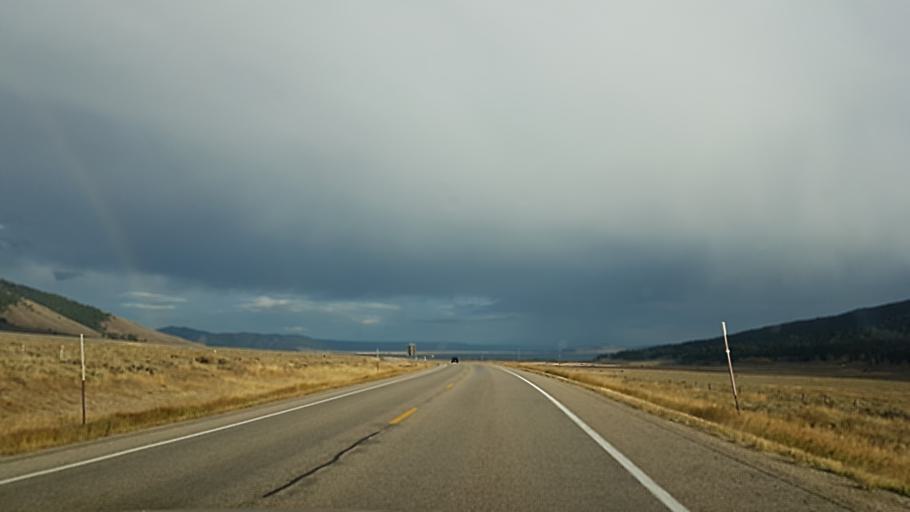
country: US
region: Montana
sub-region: Gallatin County
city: West Yellowstone
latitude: 44.6987
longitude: -111.4581
